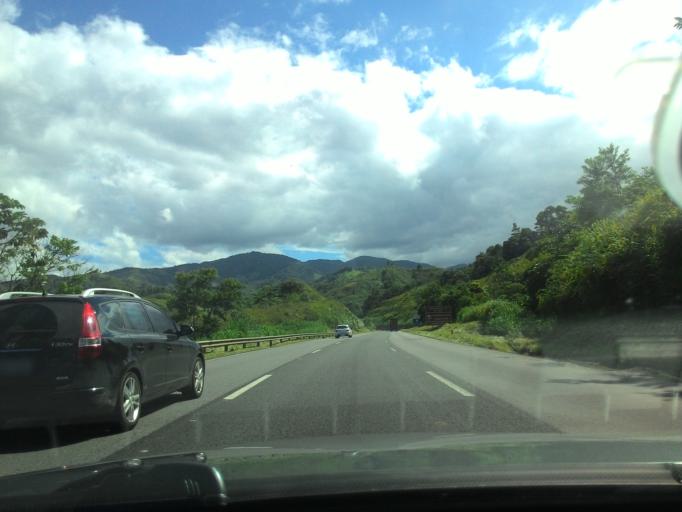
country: BR
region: Sao Paulo
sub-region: Cajati
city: Cajati
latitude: -24.8289
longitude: -48.2192
